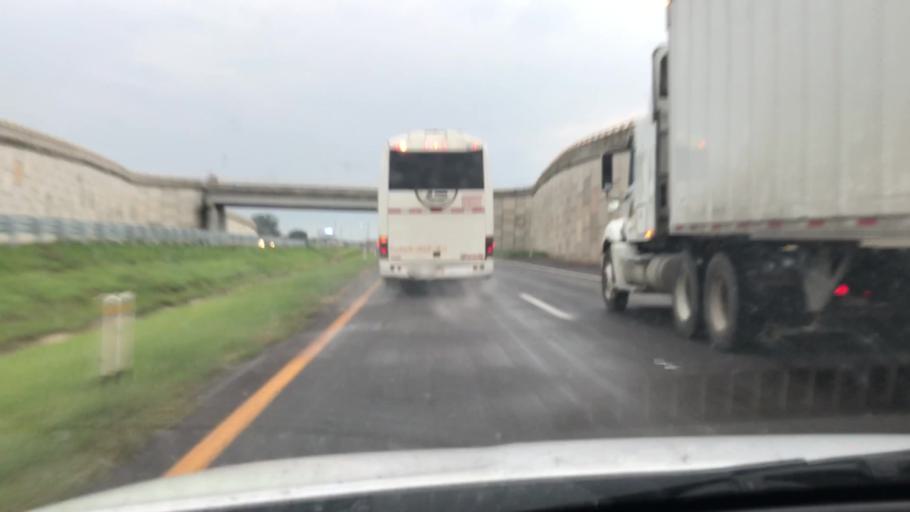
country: MX
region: Jalisco
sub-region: Zapotlanejo
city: La Mezquitera
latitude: 20.5463
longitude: -103.0309
